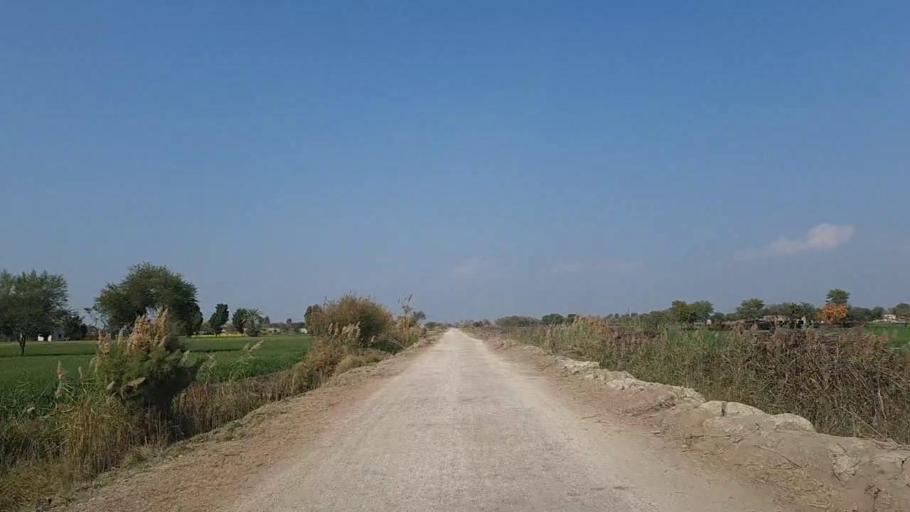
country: PK
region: Sindh
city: Jam Sahib
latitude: 26.2931
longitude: 68.5831
